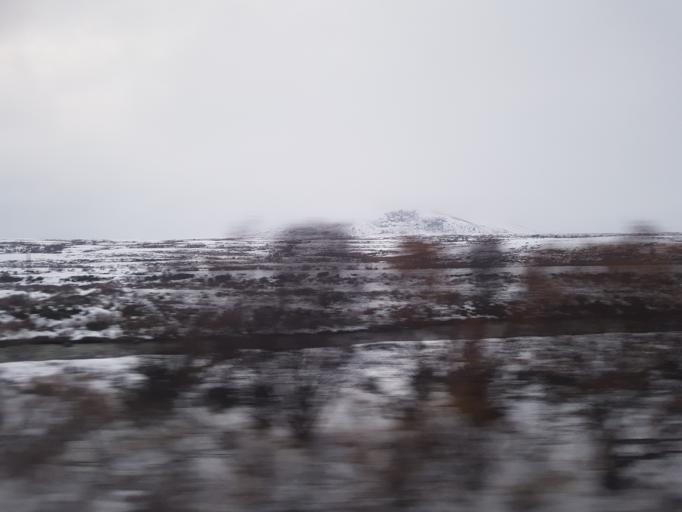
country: NO
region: Sor-Trondelag
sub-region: Oppdal
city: Oppdal
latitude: 62.2688
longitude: 9.5745
